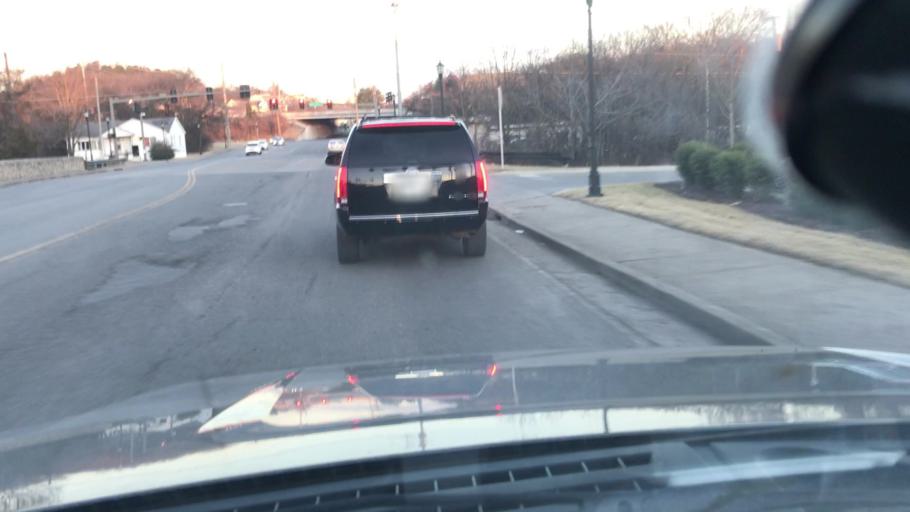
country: US
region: Tennessee
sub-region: Williamson County
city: Brentwood
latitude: 36.0331
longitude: -86.7864
